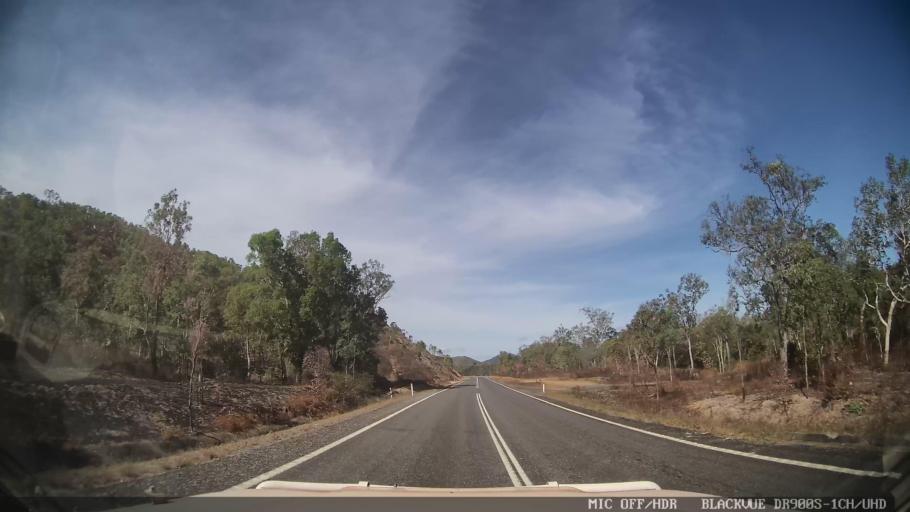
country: AU
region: Queensland
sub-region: Cook
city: Cooktown
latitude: -15.6799
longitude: 145.1696
